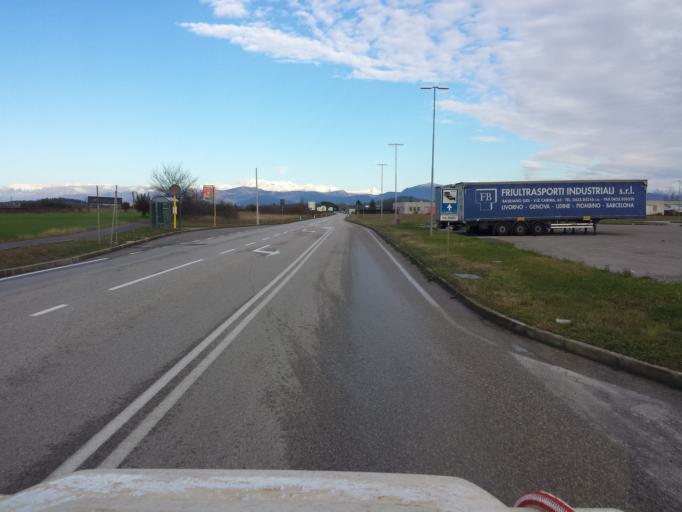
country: IT
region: Friuli Venezia Giulia
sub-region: Provincia di Udine
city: San Giovanni al Natisone
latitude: 45.9557
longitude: 13.3952
